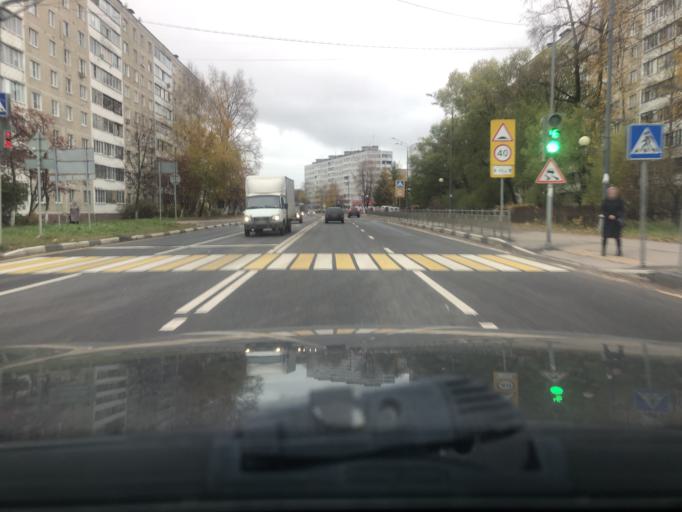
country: RU
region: Moskovskaya
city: Sergiyev Posad
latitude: 56.3245
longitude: 38.1342
